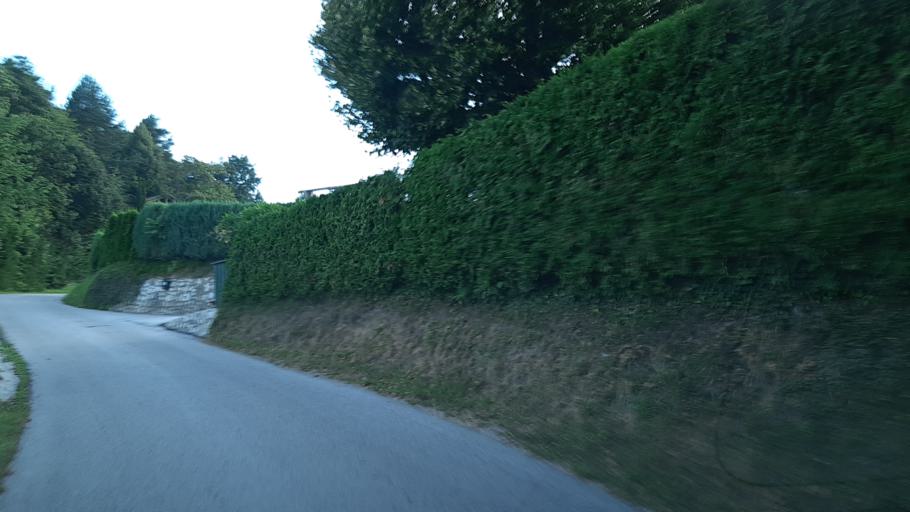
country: SI
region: Dobje
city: Dobje pri Planini
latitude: 46.1457
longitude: 15.4537
